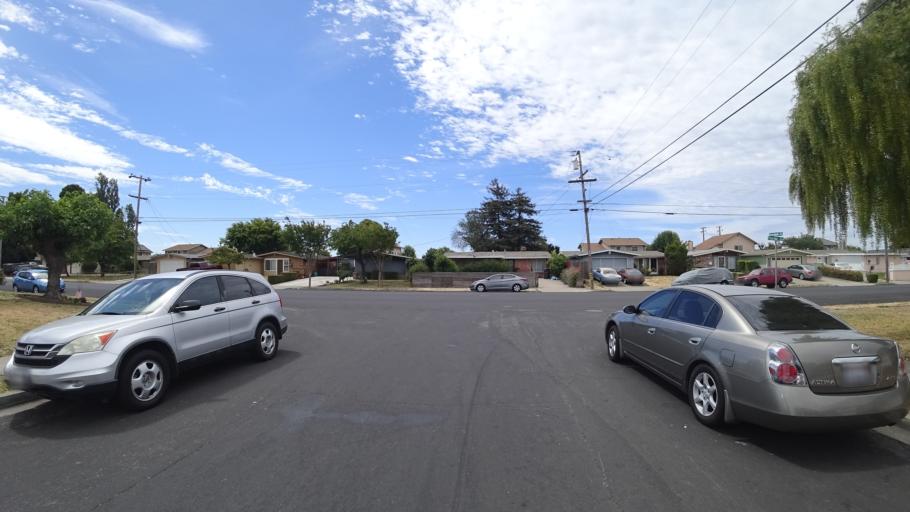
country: US
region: California
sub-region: Alameda County
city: Hayward
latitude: 37.6249
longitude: -122.0865
